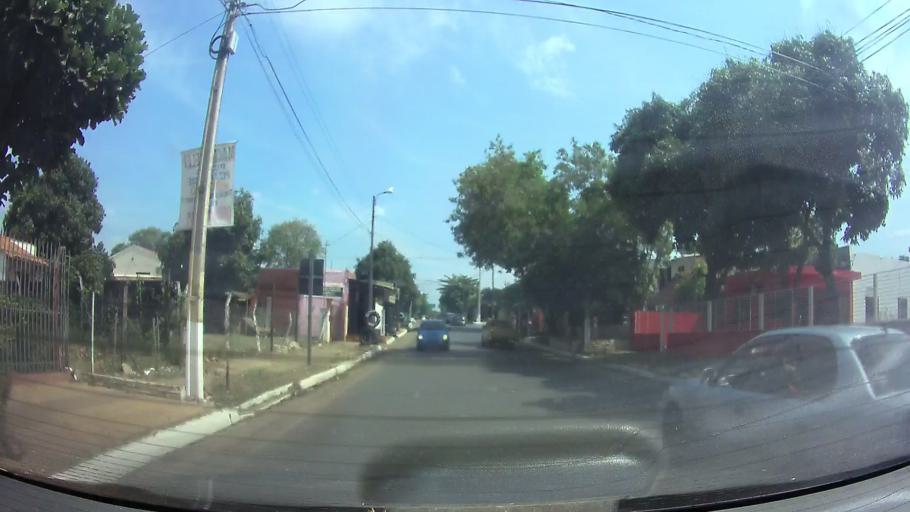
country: PY
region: Central
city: San Lorenzo
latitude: -25.3475
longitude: -57.4934
